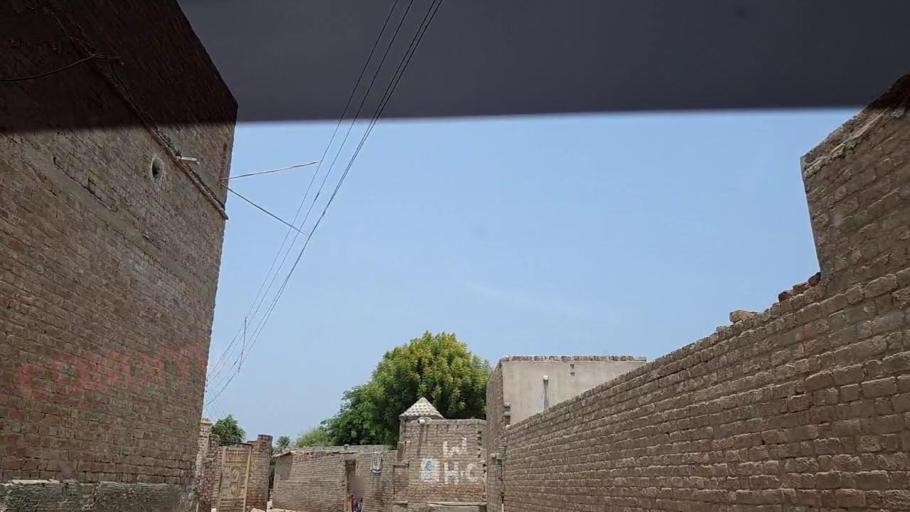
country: PK
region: Sindh
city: Adilpur
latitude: 27.8781
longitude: 69.2646
